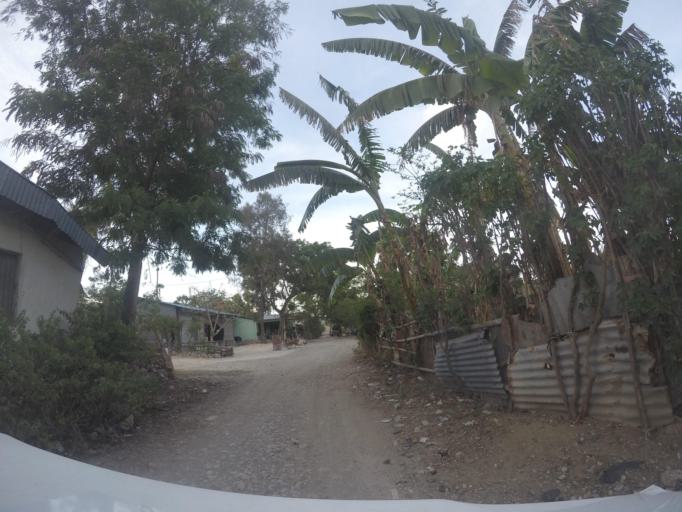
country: TL
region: Baucau
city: Baucau
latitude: -8.4758
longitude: 126.4571
